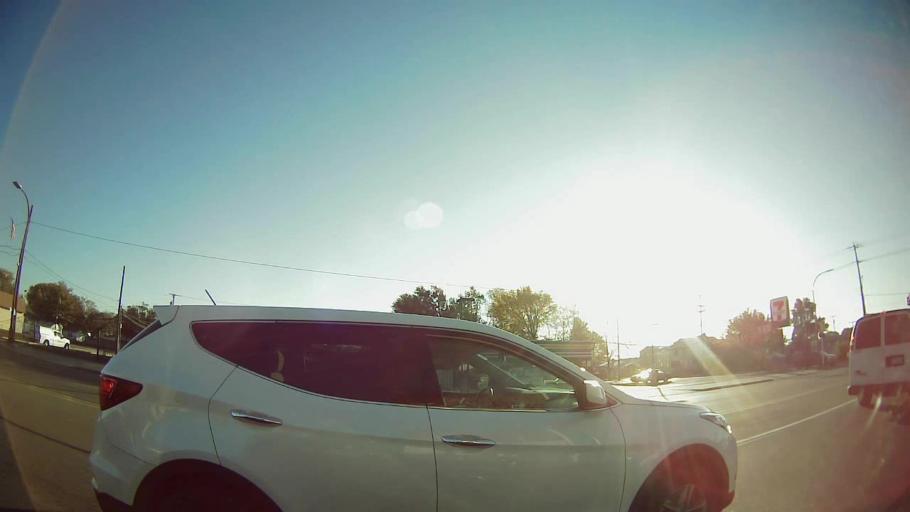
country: US
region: Michigan
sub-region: Macomb County
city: Warren
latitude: 42.4706
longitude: -83.0271
